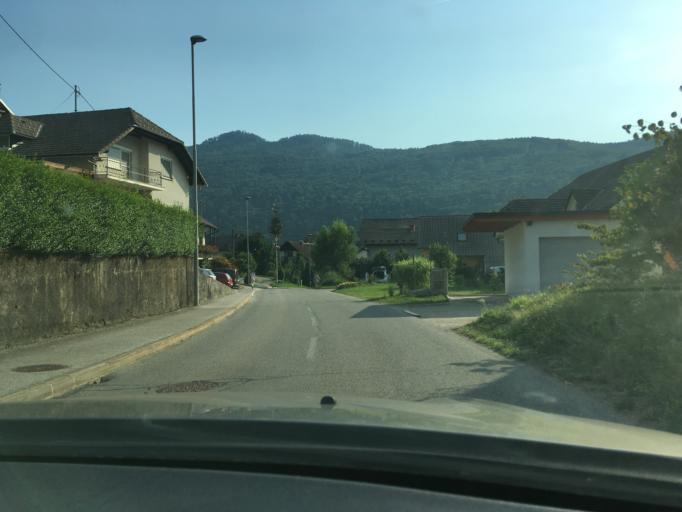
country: SI
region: Dolenjske Toplice
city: Dolenjske Toplice
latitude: 45.7607
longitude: 15.0396
